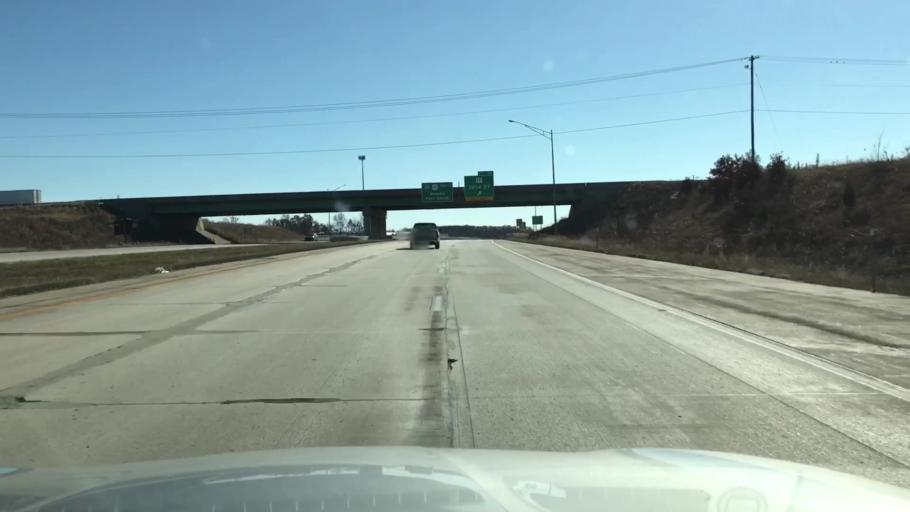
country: US
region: Missouri
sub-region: Jasper County
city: Duenweg
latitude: 37.0558
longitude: -94.4266
